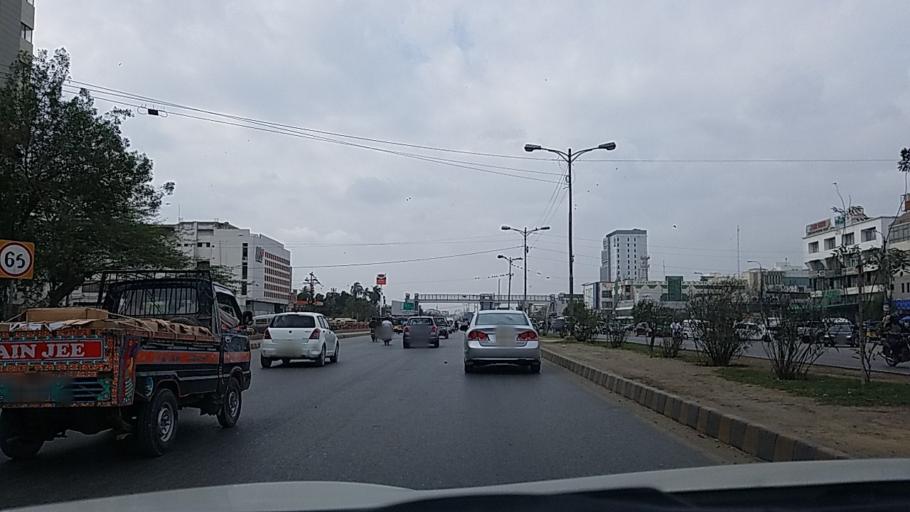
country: PK
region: Sindh
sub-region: Karachi District
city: Karachi
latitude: 24.8352
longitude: 67.0711
